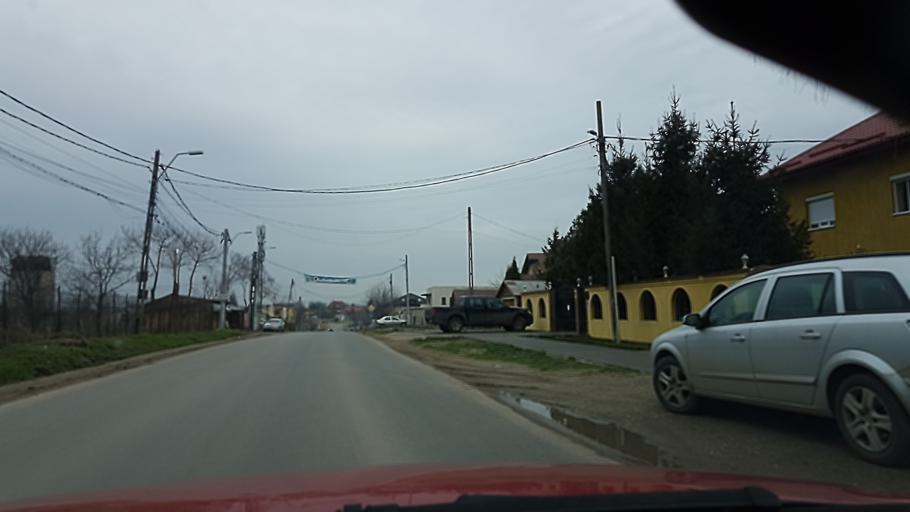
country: RO
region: Ilfov
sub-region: Comuna Tunari
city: Tunari
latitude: 44.5554
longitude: 26.1431
